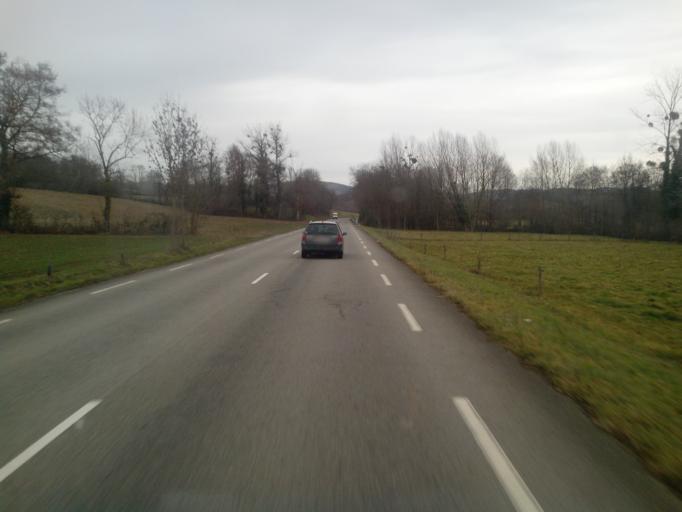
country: FR
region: Midi-Pyrenees
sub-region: Departement de l'Ariege
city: Montjoie-en-Couserans
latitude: 43.0037
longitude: 1.3540
